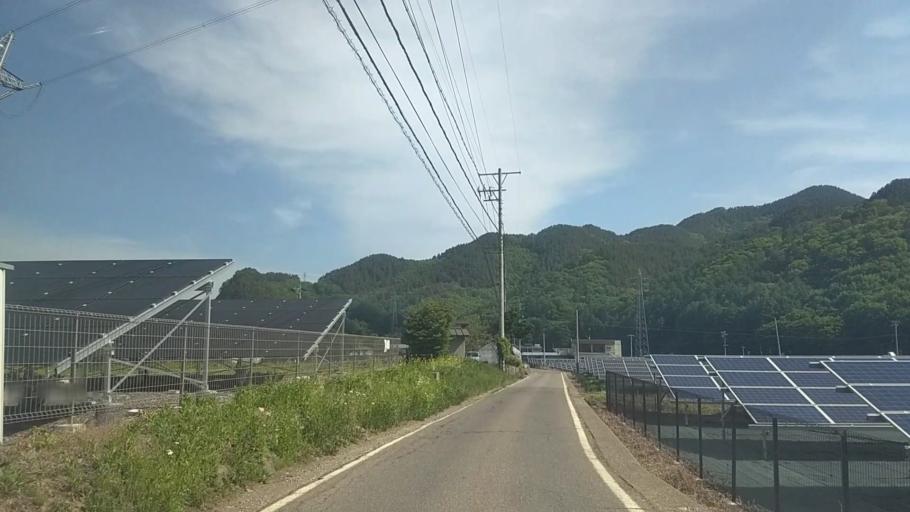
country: JP
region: Nagano
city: Saku
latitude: 36.1040
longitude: 138.4839
